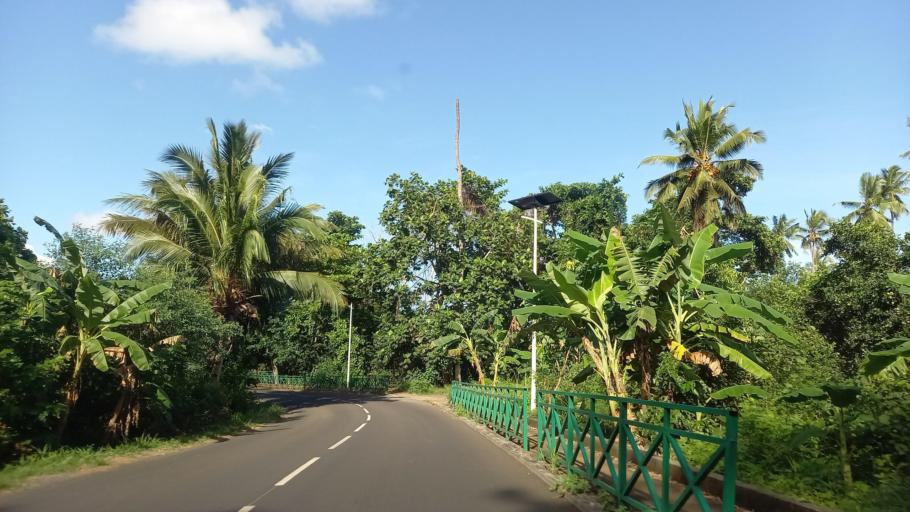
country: YT
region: Kani-Keli
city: Kani Keli
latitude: -12.9567
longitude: 45.1136
